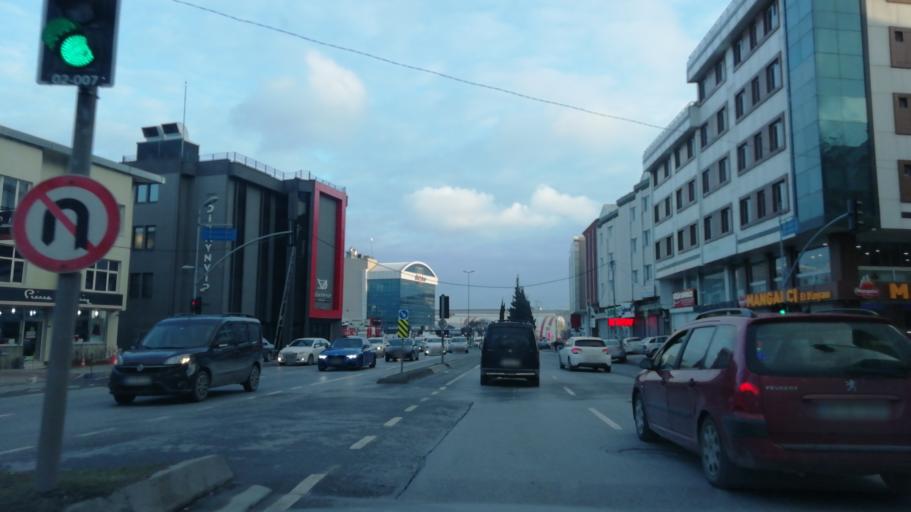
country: TR
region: Istanbul
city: Yakuplu
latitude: 41.0012
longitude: 28.7116
